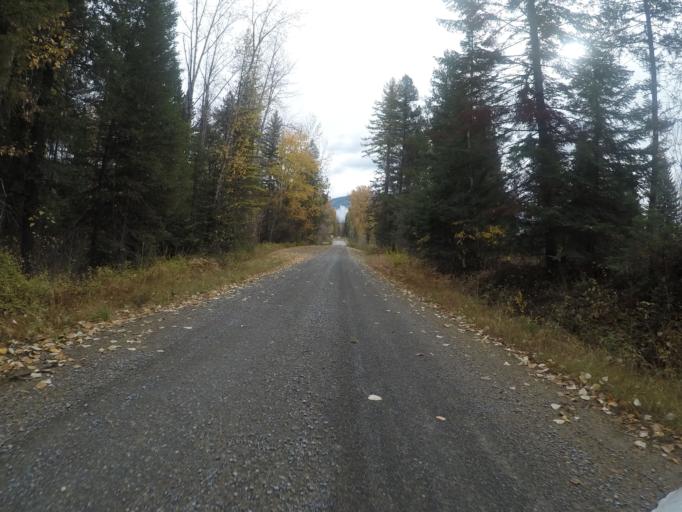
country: US
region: Montana
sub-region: Flathead County
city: Bigfork
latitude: 47.8870
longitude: -113.8624
